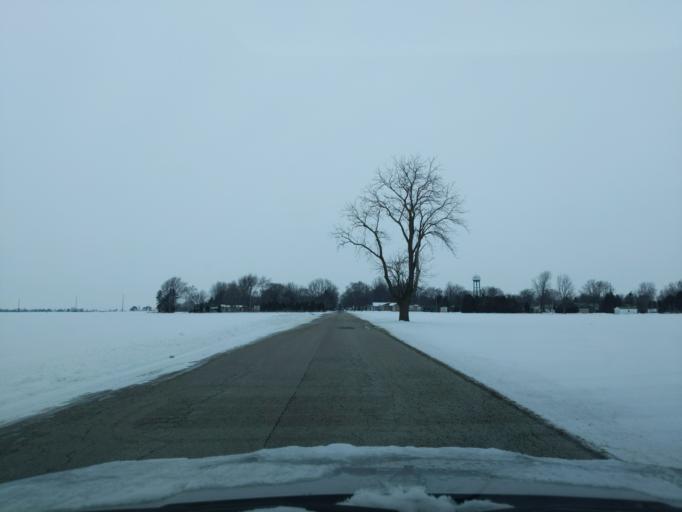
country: US
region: Indiana
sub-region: Benton County
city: Otterbein
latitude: 40.4789
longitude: -87.0932
